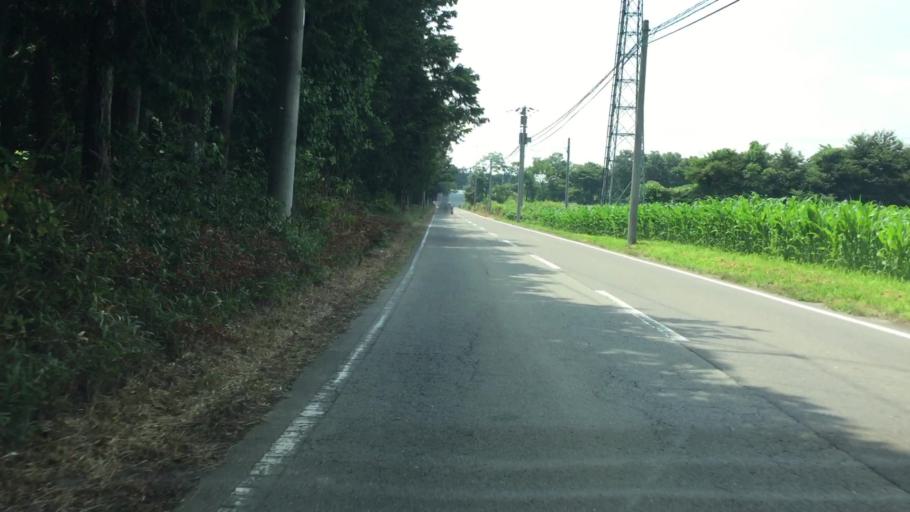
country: JP
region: Tochigi
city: Kuroiso
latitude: 36.9536
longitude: 139.9591
